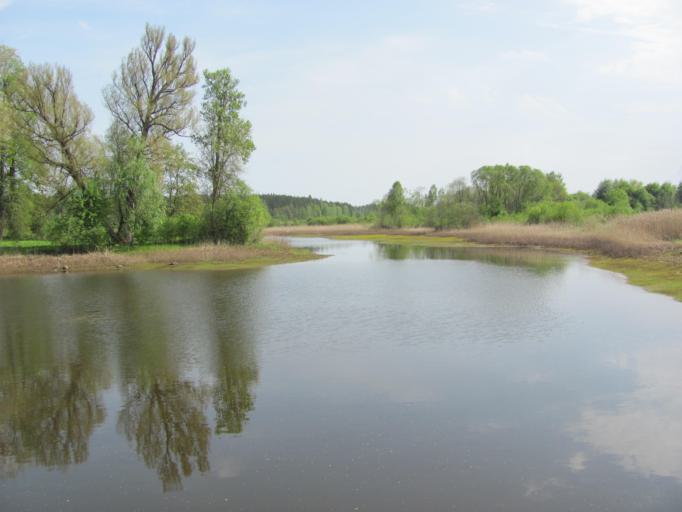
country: LT
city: Nemencine
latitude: 54.8007
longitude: 25.5141
